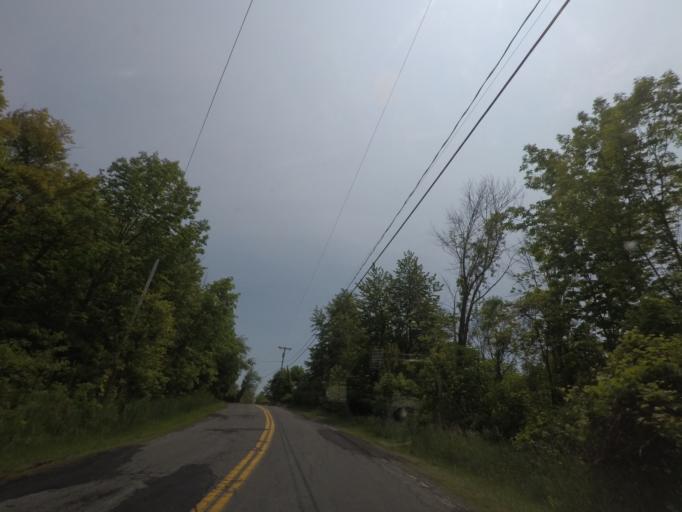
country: US
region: New York
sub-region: Rensselaer County
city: Castleton-on-Hudson
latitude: 42.4995
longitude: -73.7072
